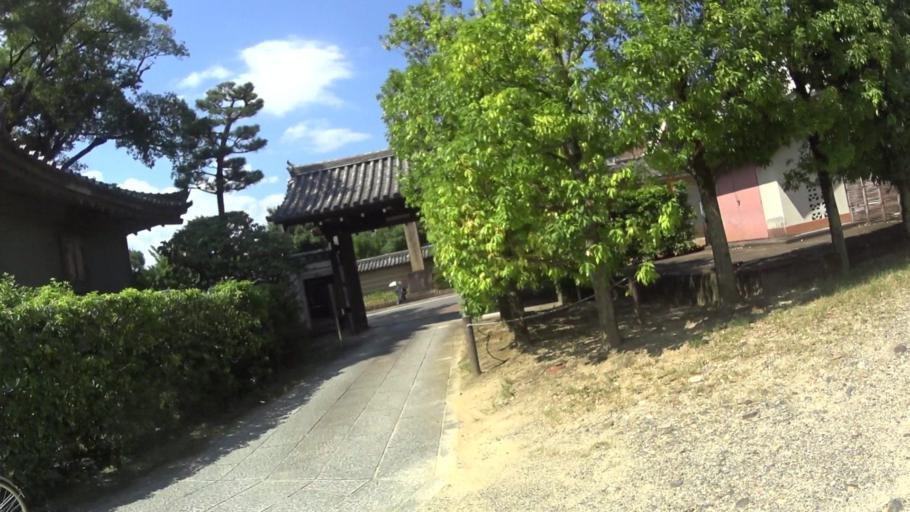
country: RU
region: Rostov
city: Remontnoye
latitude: 46.4984
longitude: 43.7823
